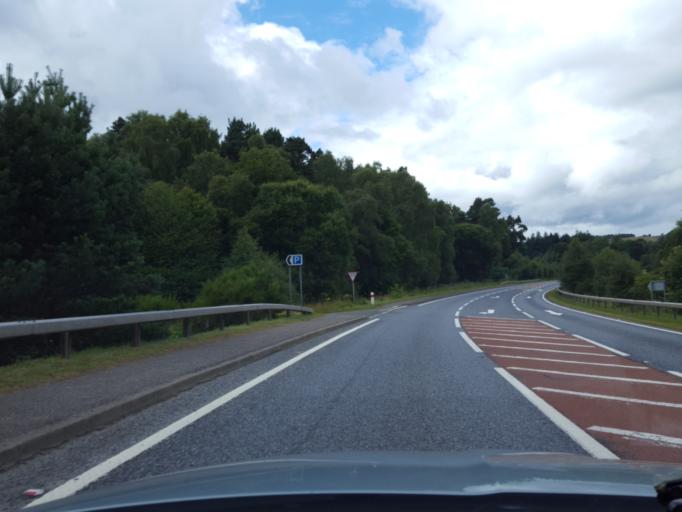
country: GB
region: Scotland
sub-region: Highland
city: Grantown on Spey
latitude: 57.3205
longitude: -3.6136
